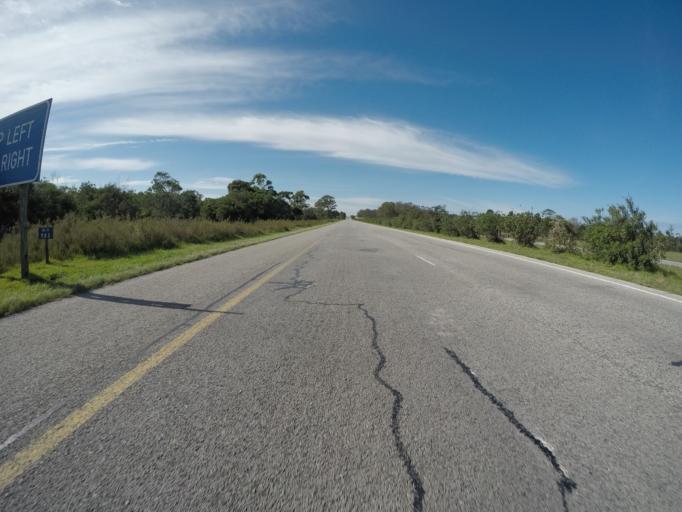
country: ZA
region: Eastern Cape
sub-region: Nelson Mandela Bay Metropolitan Municipality
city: Uitenhage
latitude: -33.9368
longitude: 25.3690
